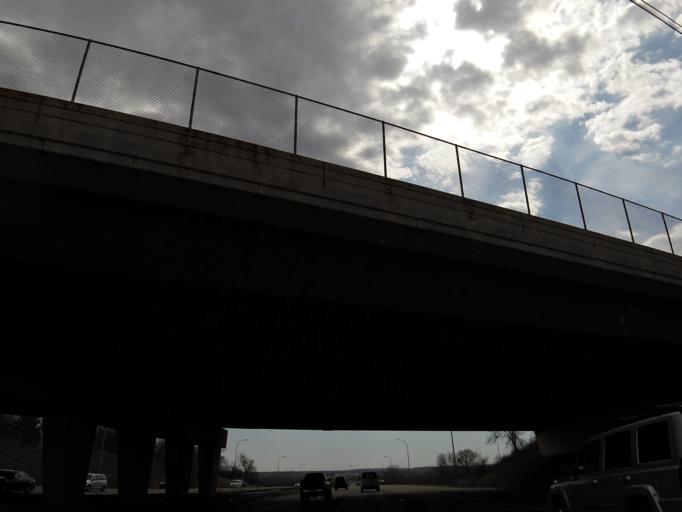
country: US
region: Minnesota
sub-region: Hennepin County
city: Bloomington
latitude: 44.8412
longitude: -93.2447
